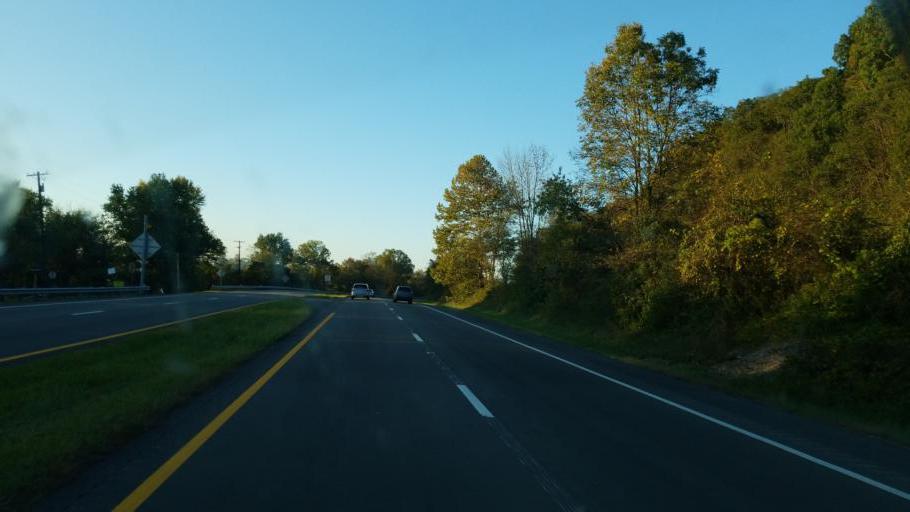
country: US
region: Ohio
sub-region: Scioto County
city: Lucasville
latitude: 38.8429
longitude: -82.9850
